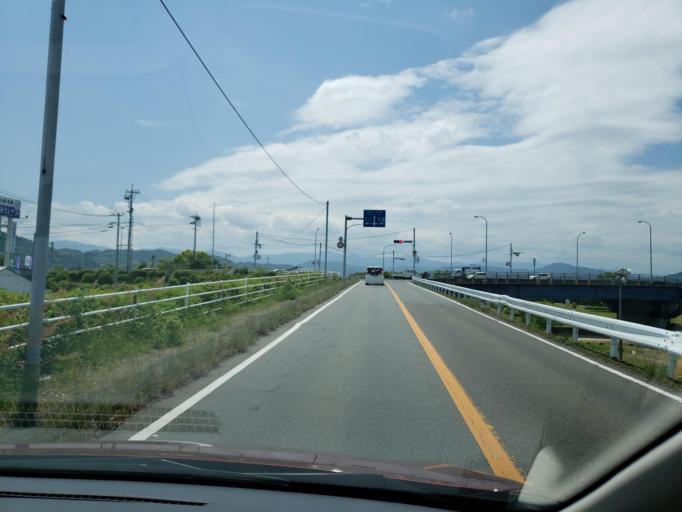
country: JP
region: Tokushima
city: Tokushima-shi
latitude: 34.0824
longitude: 134.5049
